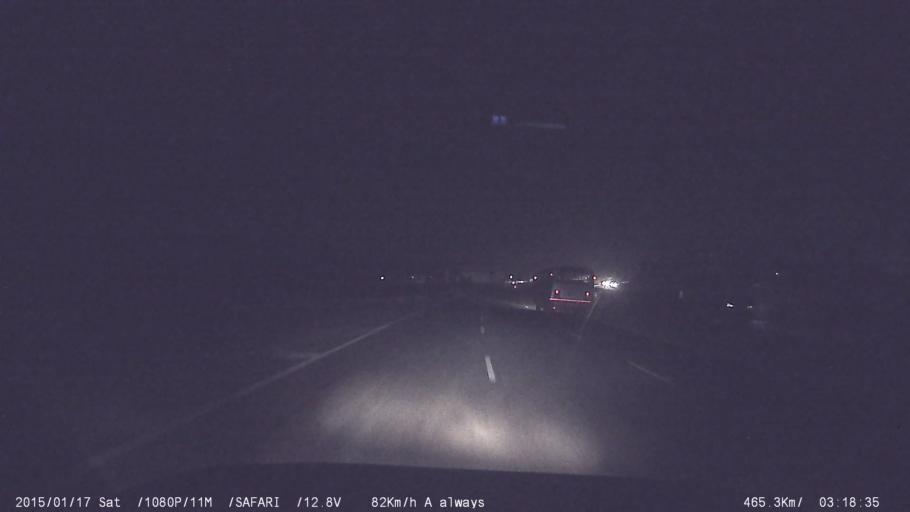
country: IN
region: Tamil Nadu
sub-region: Krishnagiri
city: Kelamangalam
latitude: 12.6784
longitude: 77.9632
